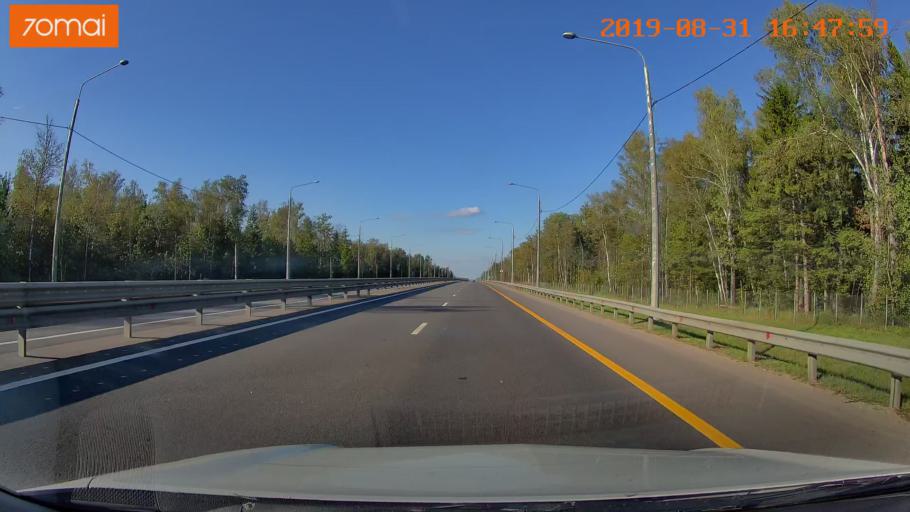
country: RU
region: Kaluga
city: Pyatovskiy
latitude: 54.6640
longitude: 36.1432
